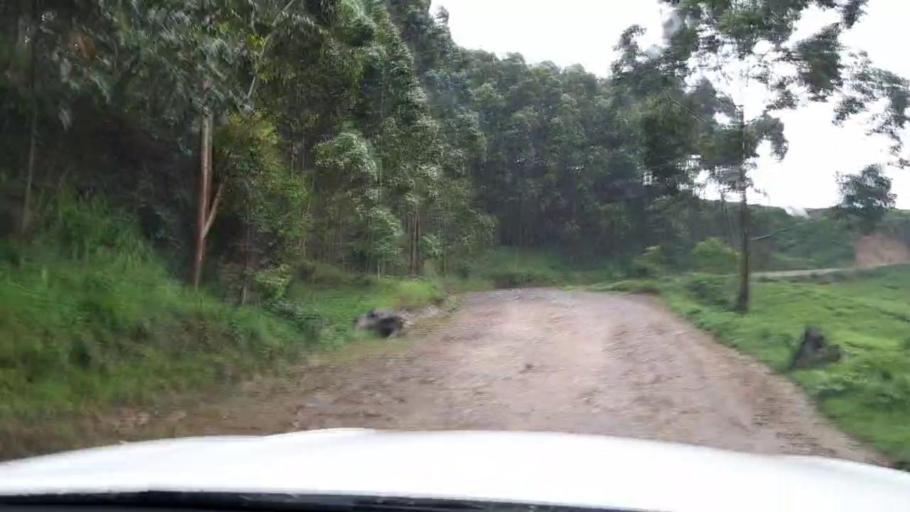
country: RW
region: Western Province
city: Cyangugu
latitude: -2.4584
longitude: 29.0371
